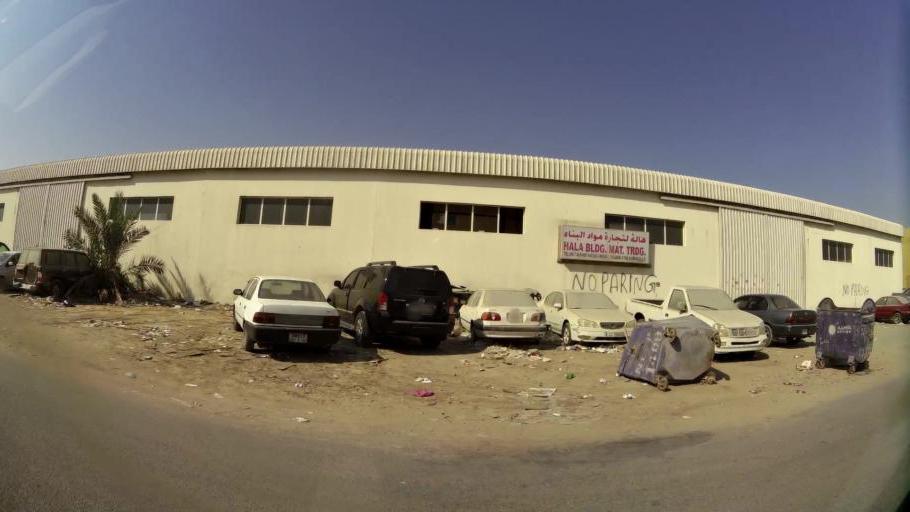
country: AE
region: Ajman
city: Ajman
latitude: 25.4377
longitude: 55.5142
